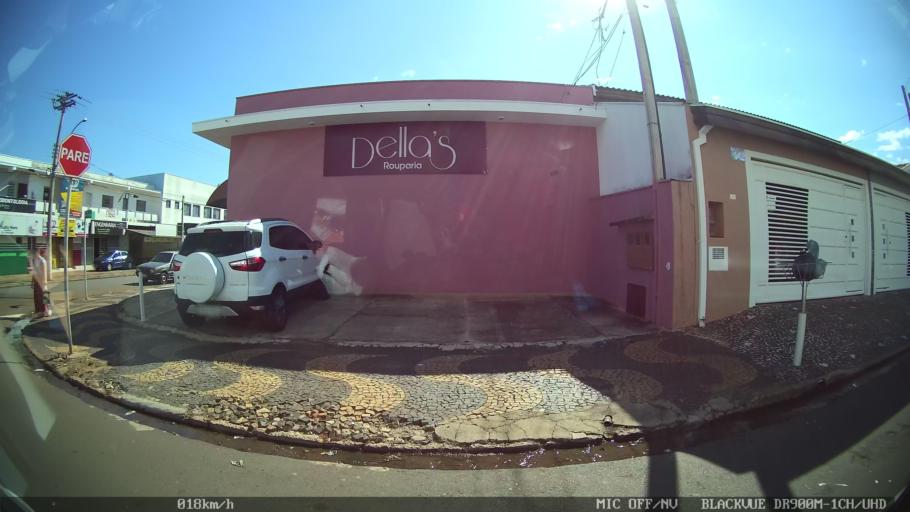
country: BR
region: Sao Paulo
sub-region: Santa Barbara D'Oeste
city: Santa Barbara d'Oeste
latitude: -22.7378
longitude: -47.3795
